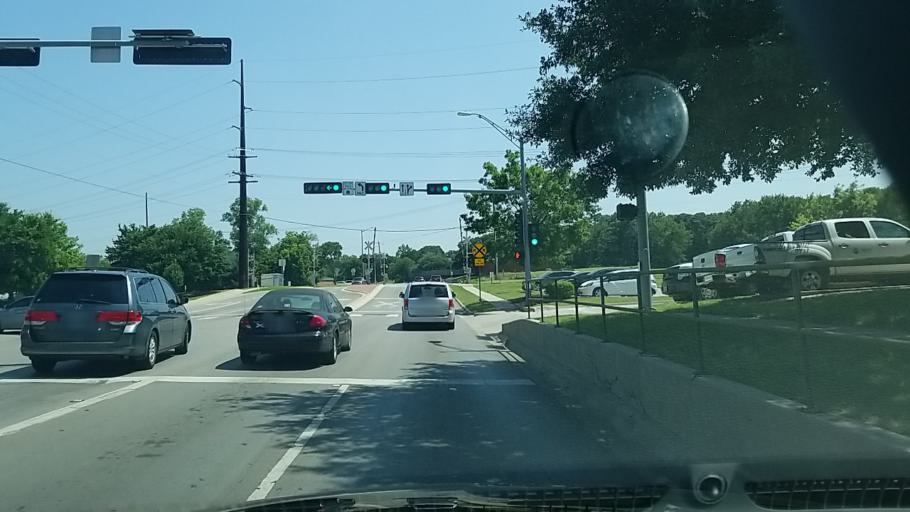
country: US
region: Texas
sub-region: Denton County
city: Denton
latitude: 33.2005
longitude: -97.1128
